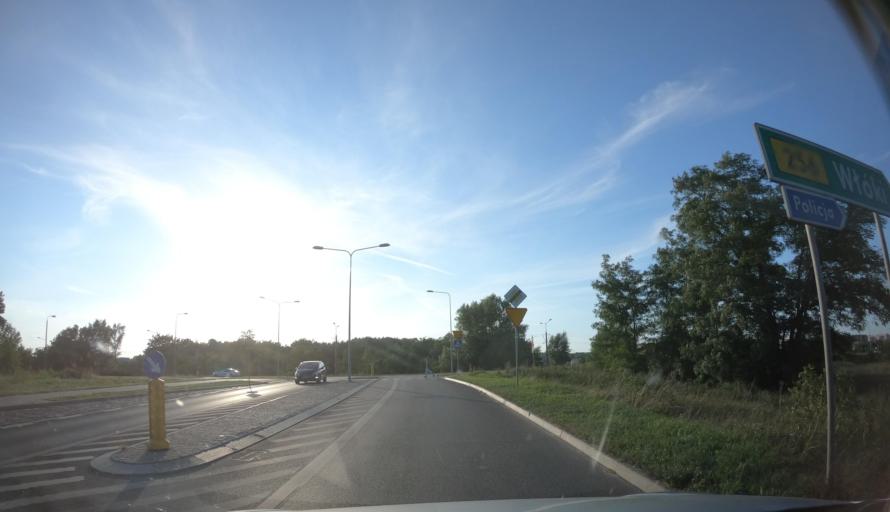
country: PL
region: Kujawsko-Pomorskie
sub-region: Bydgoszcz
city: Fordon
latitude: 53.1538
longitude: 18.1616
